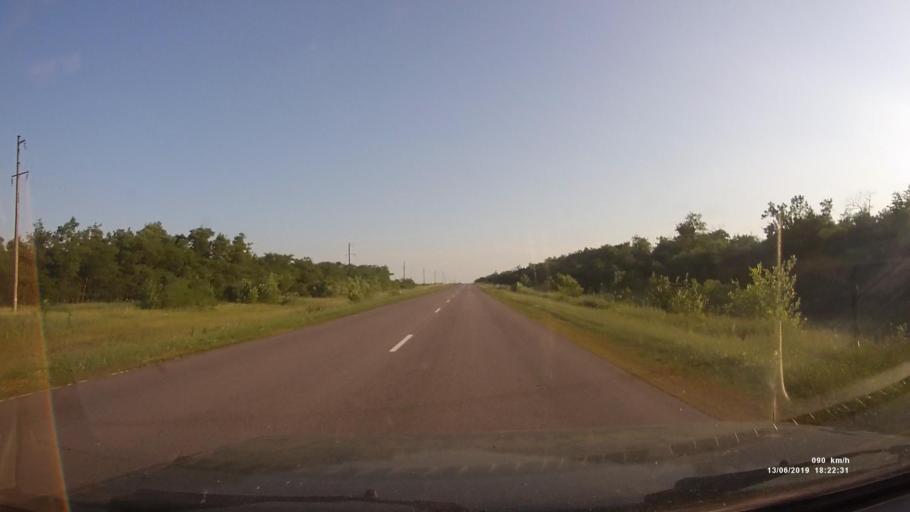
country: RU
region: Rostov
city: Kazanskaya
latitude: 49.8576
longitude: 41.2779
